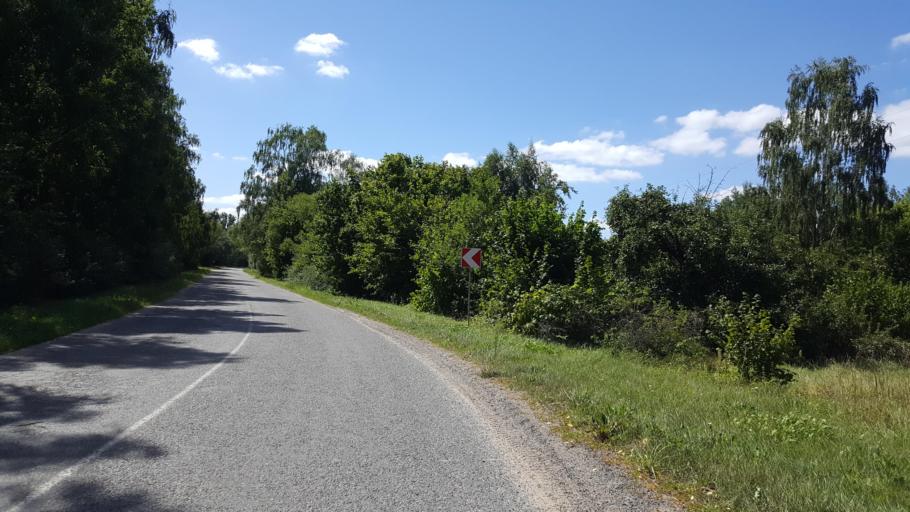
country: BY
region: Brest
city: Horad Kobryn
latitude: 52.2994
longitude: 24.3535
